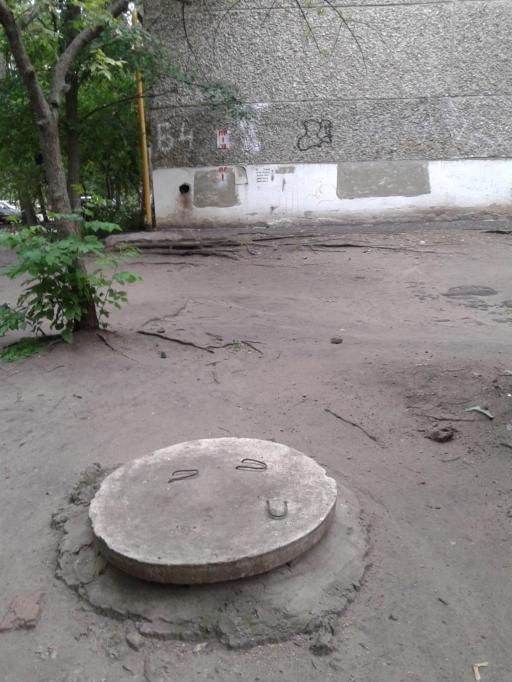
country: RU
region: Voronezj
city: Pridonskoy
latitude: 51.6561
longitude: 39.1075
